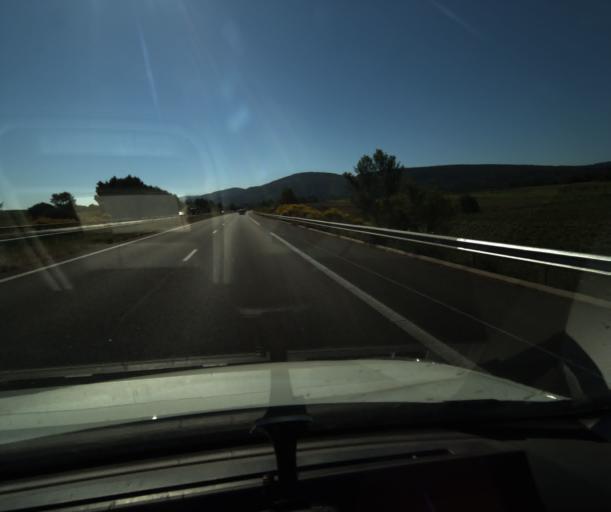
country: FR
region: Languedoc-Roussillon
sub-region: Departement de l'Aude
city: Trebes
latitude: 43.1909
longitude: 2.4588
